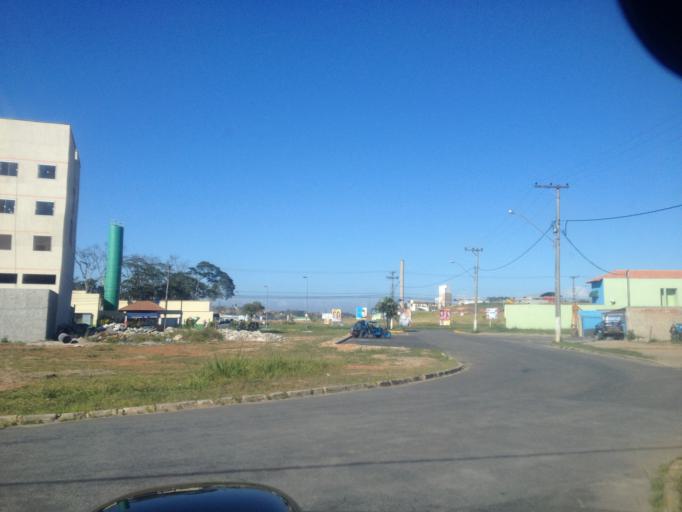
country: BR
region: Rio de Janeiro
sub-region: Porto Real
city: Porto Real
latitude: -22.4165
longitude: -44.3032
